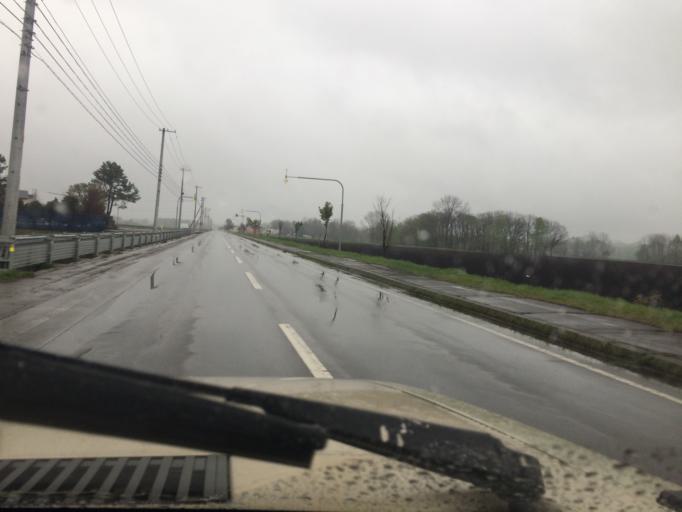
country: JP
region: Hokkaido
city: Obihiro
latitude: 42.8676
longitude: 143.0183
